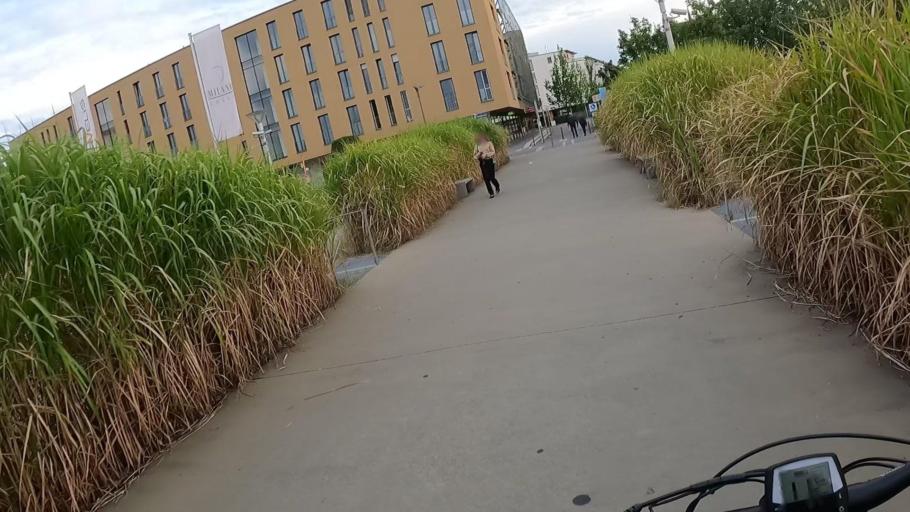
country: DE
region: Baden-Wuerttemberg
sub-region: Freiburg Region
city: Radolfzell am Bodensee
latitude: 47.7416
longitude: 8.9723
